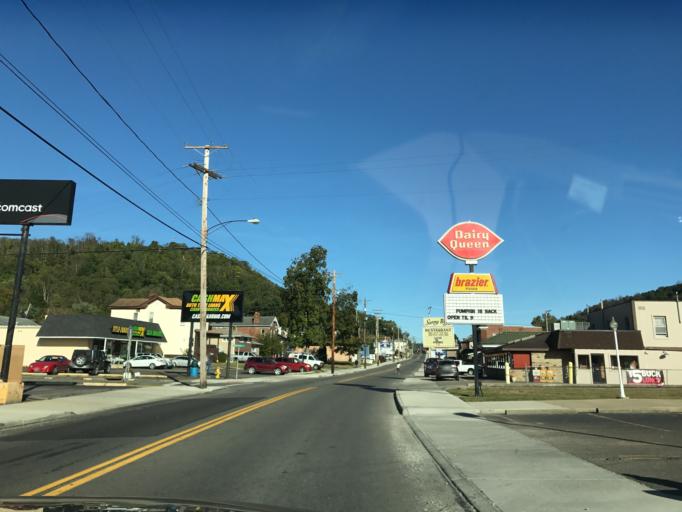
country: US
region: Ohio
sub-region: Belmont County
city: Wolfhurst
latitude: 40.0705
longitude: -80.7621
